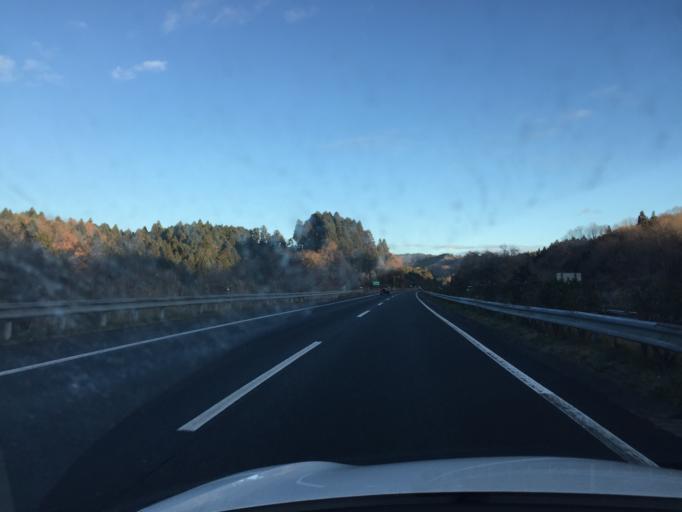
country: JP
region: Ibaraki
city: Kitaibaraki
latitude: 36.8227
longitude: 140.7300
